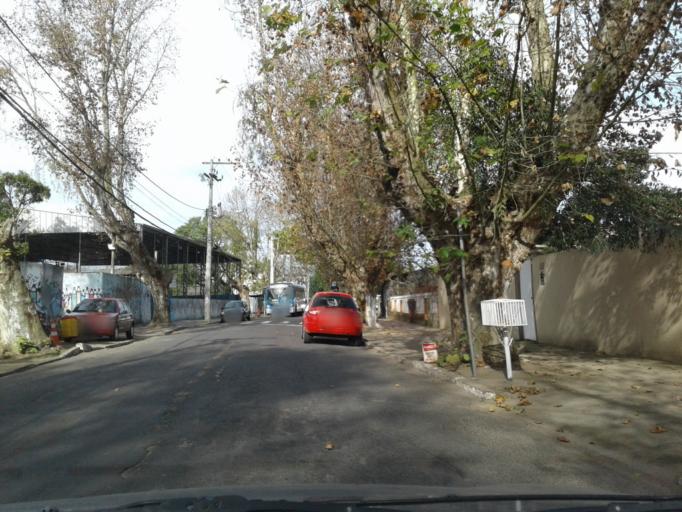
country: BR
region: Rio Grande do Sul
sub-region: Porto Alegre
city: Porto Alegre
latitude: -30.0138
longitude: -51.2601
